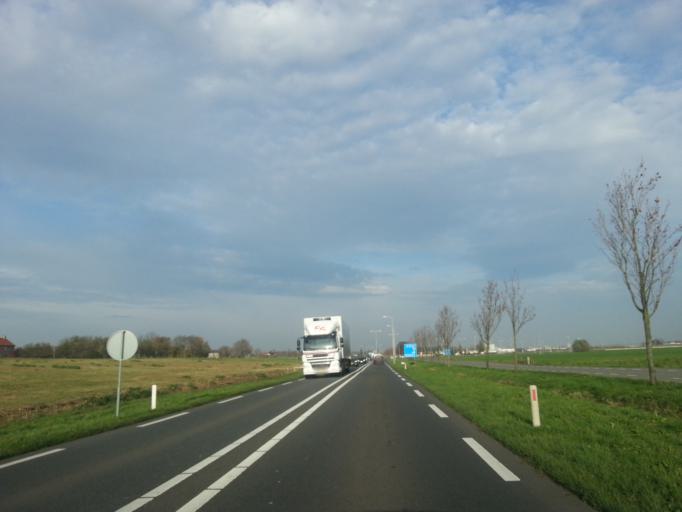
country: NL
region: South Holland
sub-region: Gemeente Lansingerland
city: Bleiswijk
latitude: 51.9957
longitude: 4.5946
